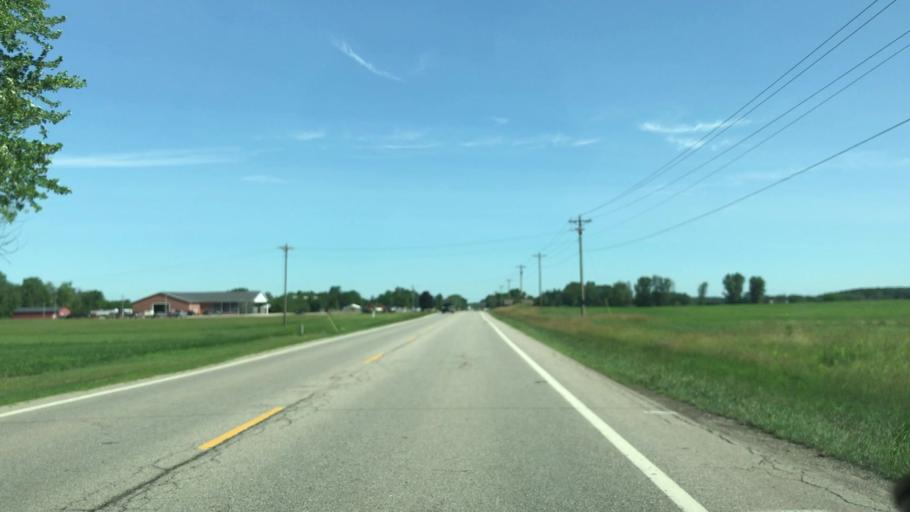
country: US
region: Ohio
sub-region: Huron County
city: Greenwich
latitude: 41.0227
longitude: -82.4850
